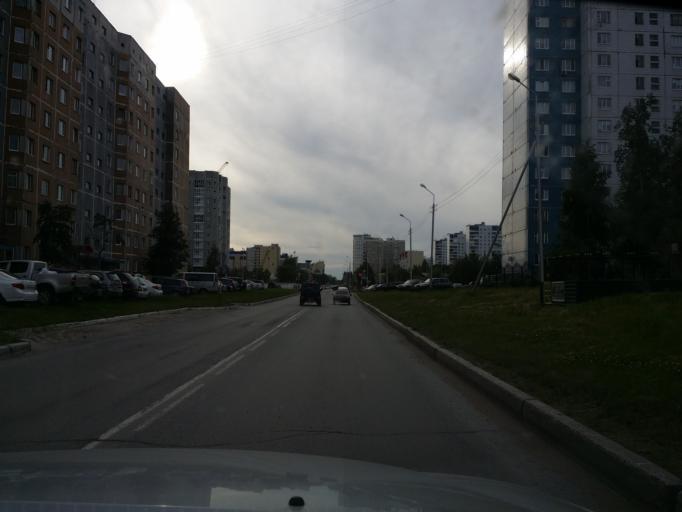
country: RU
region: Khanty-Mansiyskiy Avtonomnyy Okrug
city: Nizhnevartovsk
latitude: 60.9318
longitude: 76.5909
